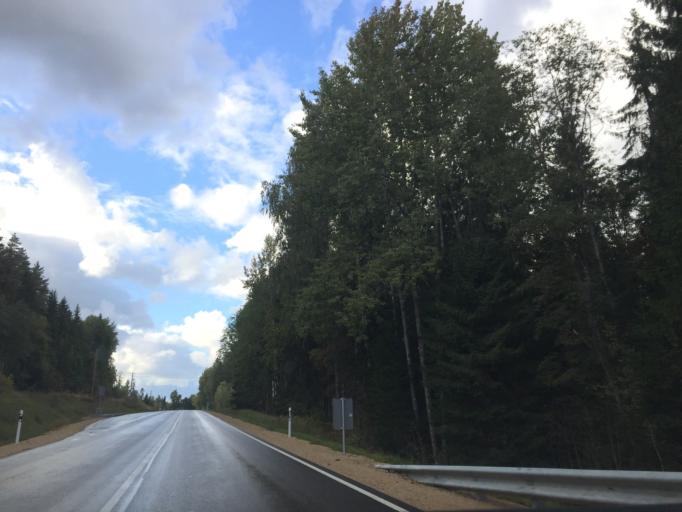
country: LV
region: Ligatne
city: Ligatne
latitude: 57.1594
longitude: 25.0598
